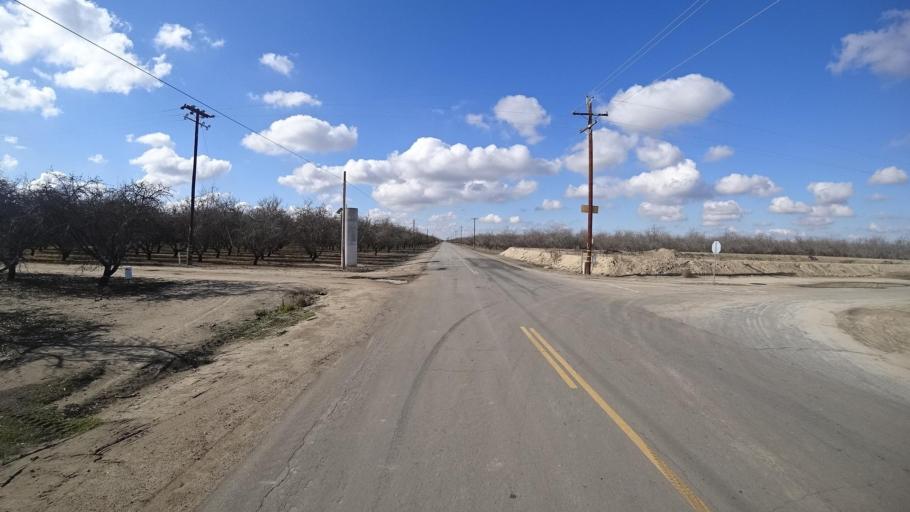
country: US
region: California
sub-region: Kern County
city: McFarland
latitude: 35.6887
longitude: -119.3120
